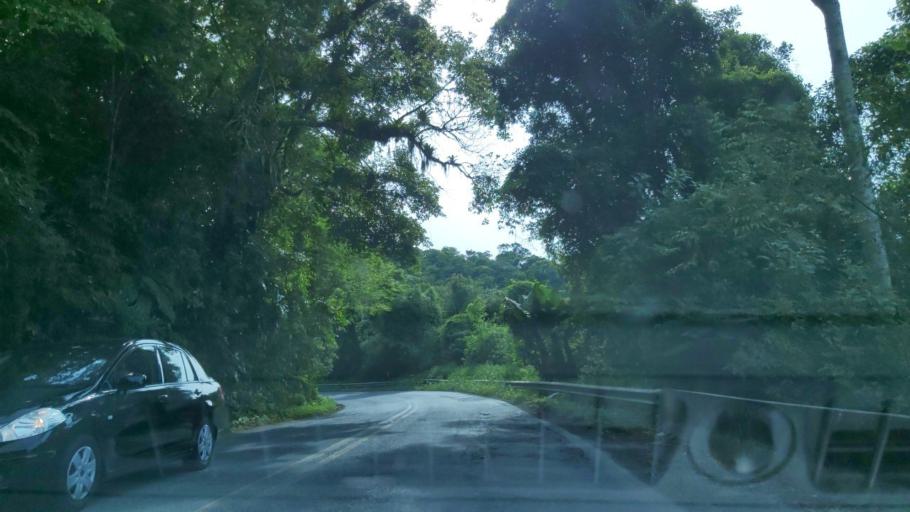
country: BR
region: Sao Paulo
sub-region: Juquia
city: Juquia
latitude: -24.0844
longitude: -47.6090
